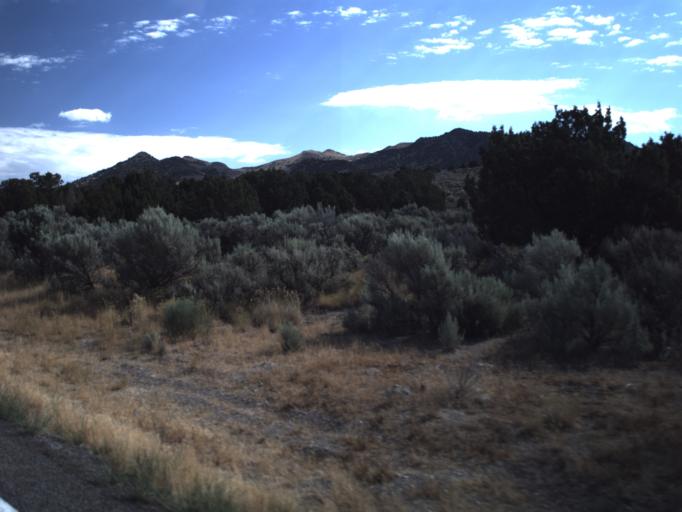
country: US
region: Utah
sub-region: Juab County
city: Mona
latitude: 39.8165
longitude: -112.1421
